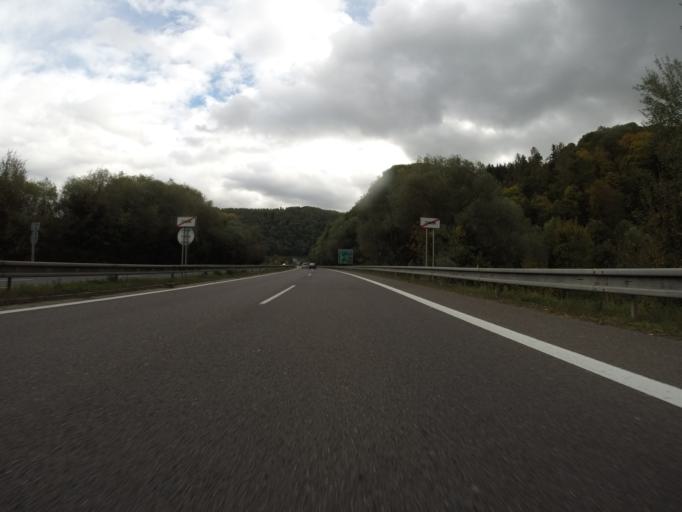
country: SK
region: Banskobystricky
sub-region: Okres Banska Bystrica
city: Zvolen
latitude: 48.5699
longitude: 19.1046
